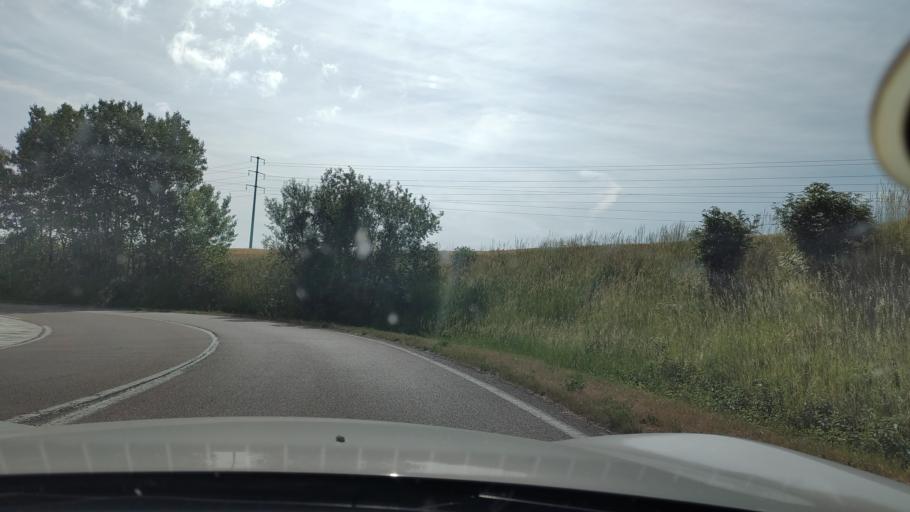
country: FR
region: Champagne-Ardenne
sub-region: Departement de l'Aube
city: Nogent-sur-Seine
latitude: 48.4899
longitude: 3.5218
